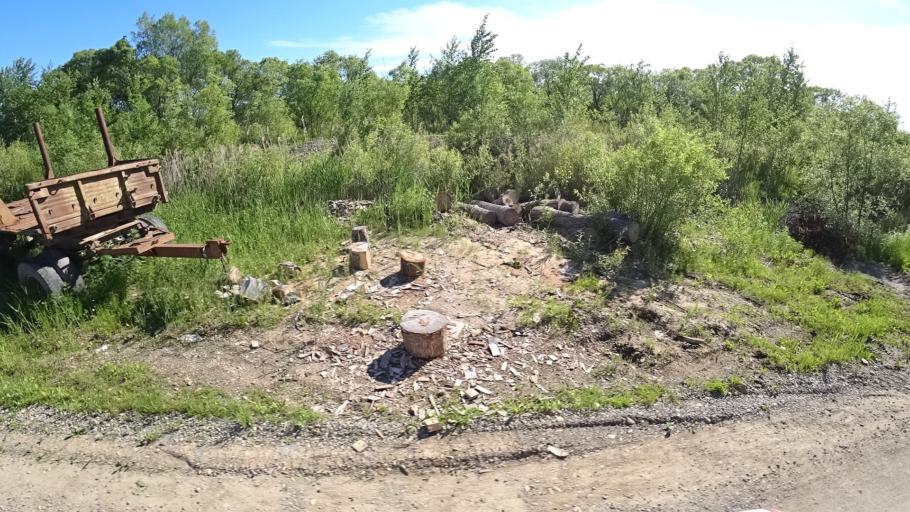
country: RU
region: Khabarovsk Krai
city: Khor
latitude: 47.8859
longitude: 135.0169
